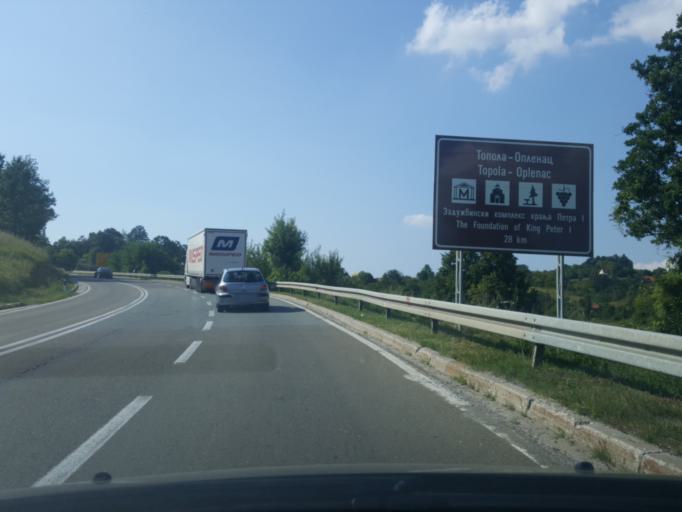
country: RS
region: Central Serbia
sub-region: Moravicki Okrug
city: Gornji Milanovac
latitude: 44.1160
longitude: 20.4850
